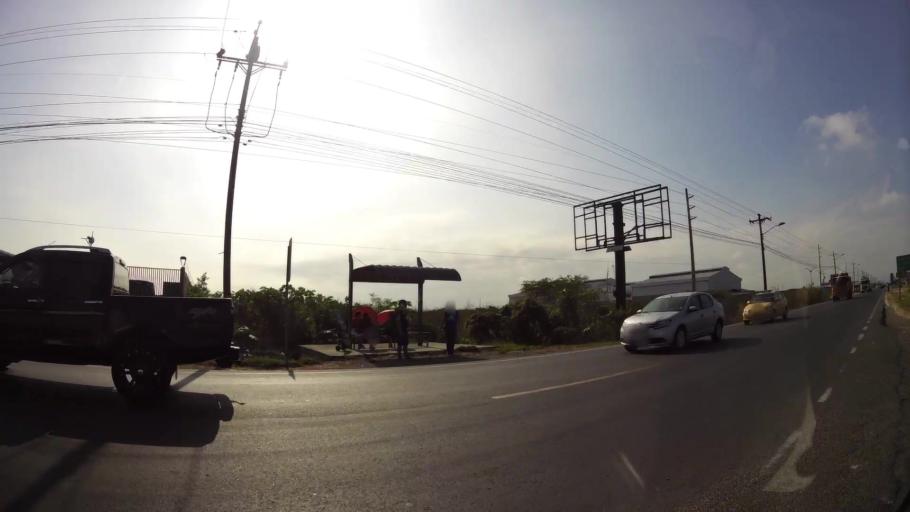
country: EC
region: Guayas
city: Eloy Alfaro
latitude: -2.1989
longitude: -79.8182
